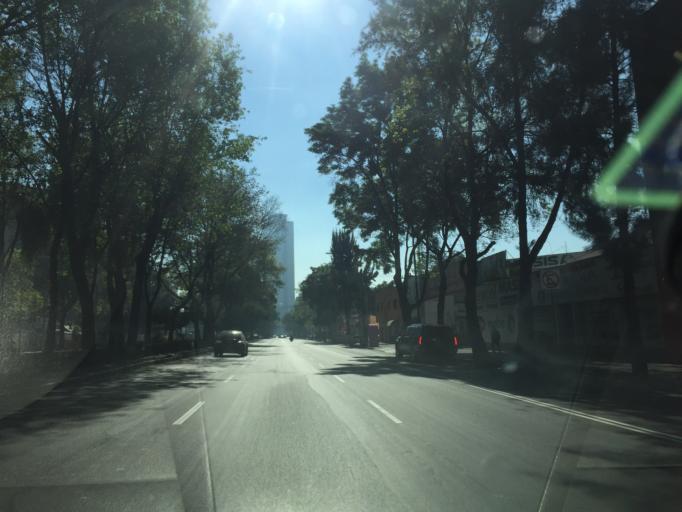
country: MX
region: Mexico City
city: Miguel Hidalgo
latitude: 19.4465
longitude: -99.1811
